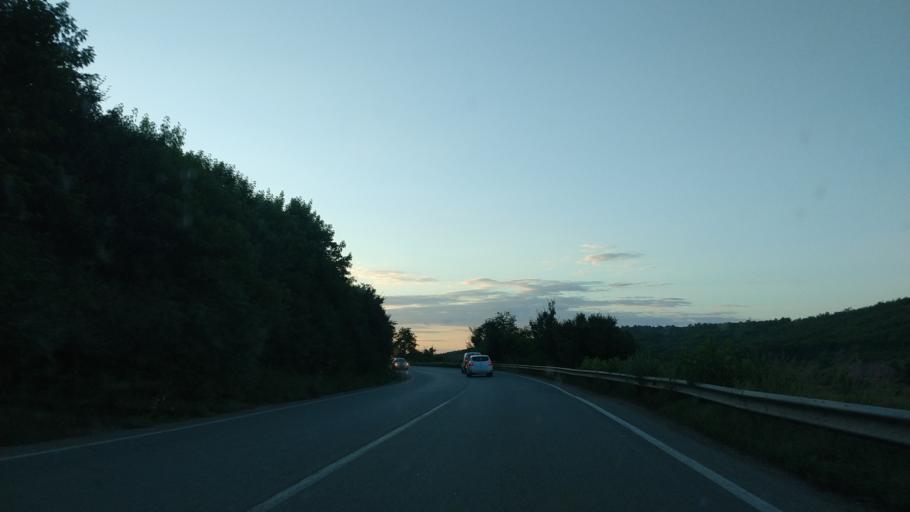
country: RO
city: Vanatori
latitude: 47.2143
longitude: 27.5506
